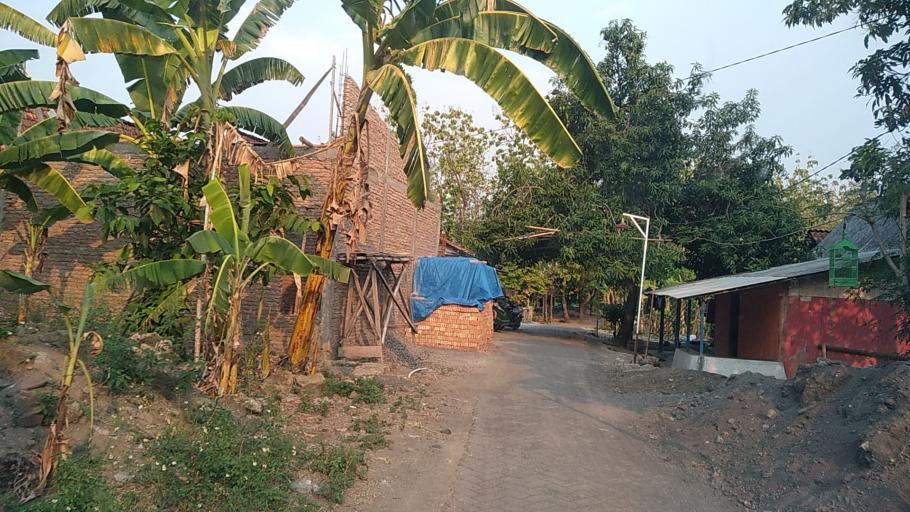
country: ID
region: Central Java
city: Mranggen
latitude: -7.0659
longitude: 110.4826
